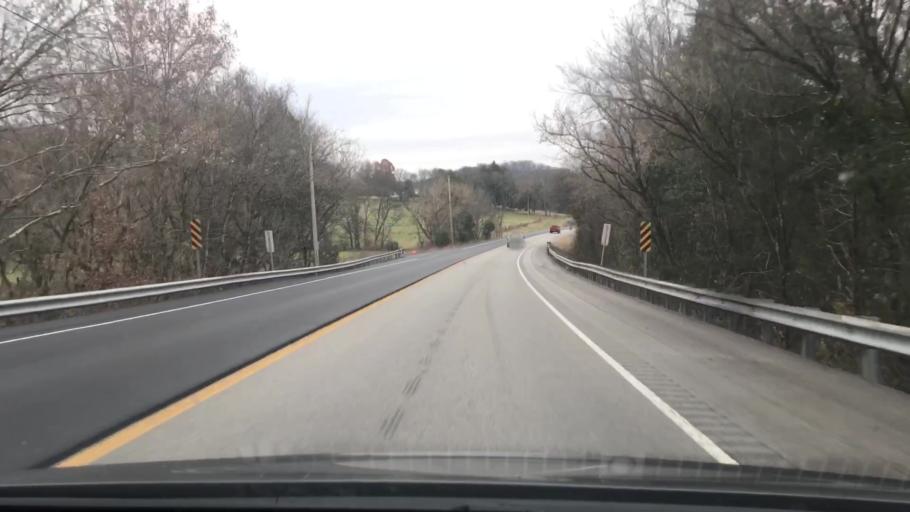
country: US
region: Tennessee
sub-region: Smith County
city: Carthage
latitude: 36.3186
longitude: -86.0121
